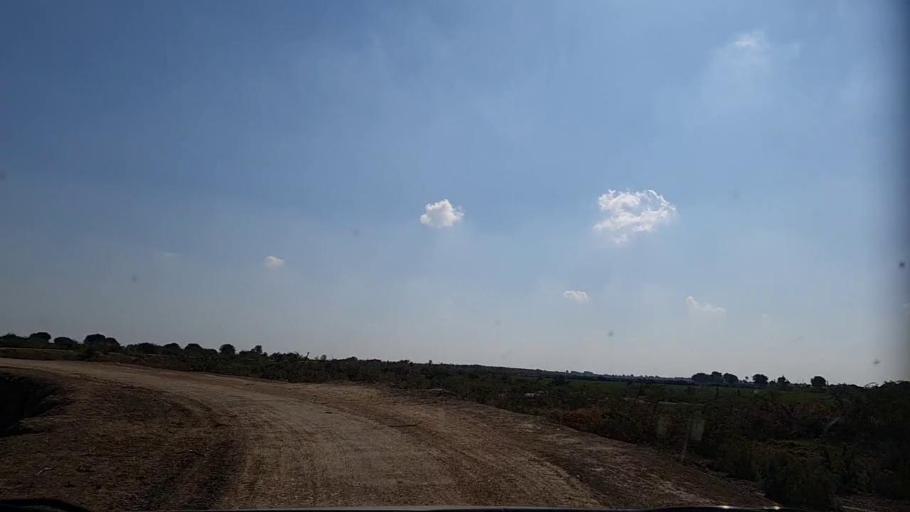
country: PK
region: Sindh
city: Pithoro
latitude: 25.6869
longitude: 69.4467
